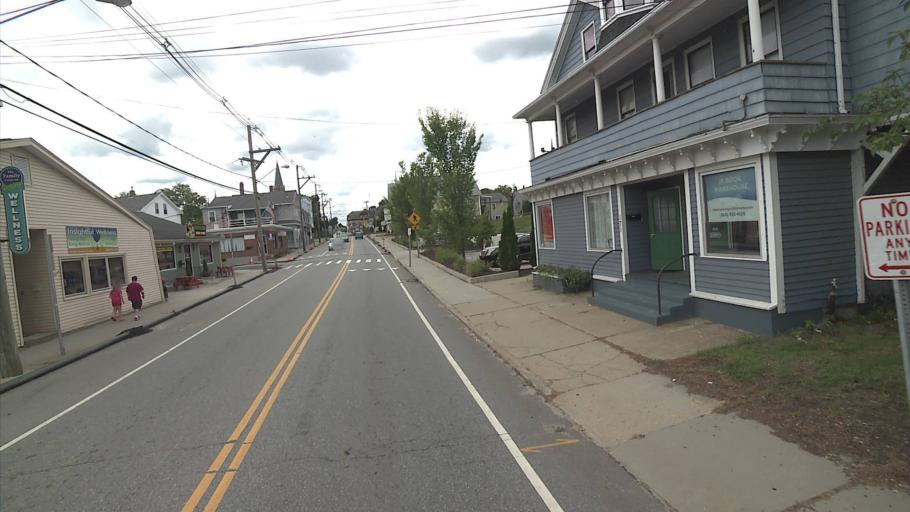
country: US
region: Connecticut
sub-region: Windham County
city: Putnam
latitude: 41.9237
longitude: -71.9091
